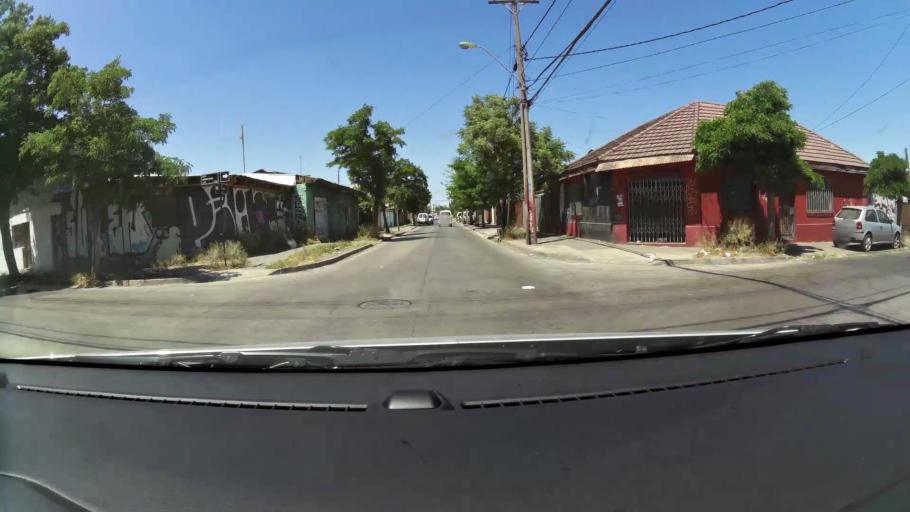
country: CL
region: Santiago Metropolitan
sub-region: Provincia de Santiago
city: La Pintana
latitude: -33.5635
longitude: -70.6626
